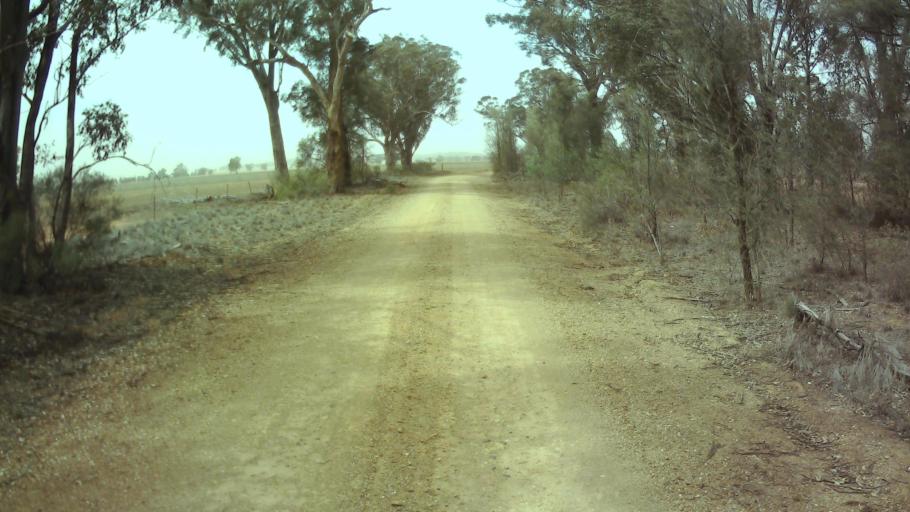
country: AU
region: New South Wales
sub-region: Weddin
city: Grenfell
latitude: -33.7170
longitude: 147.9693
